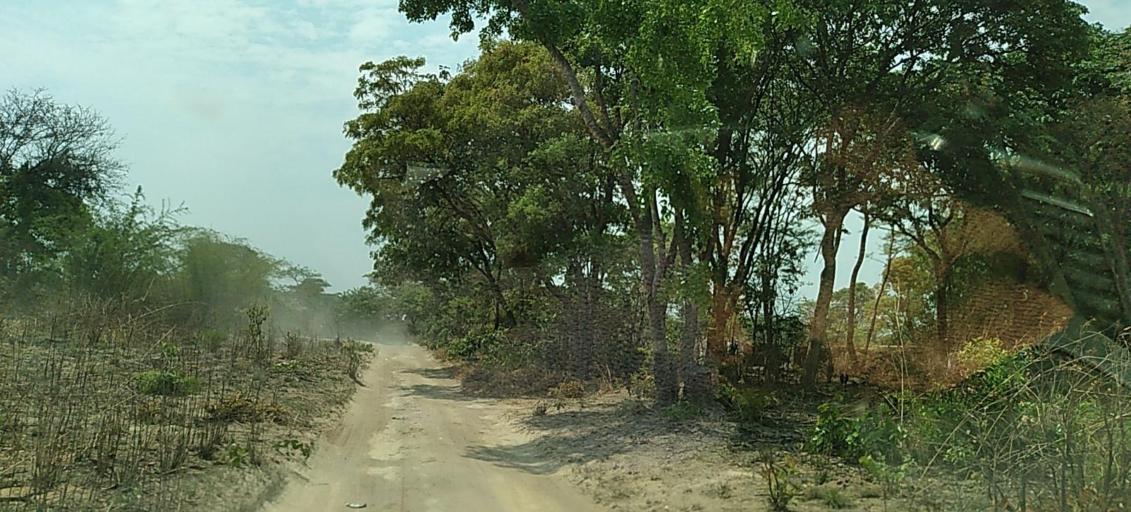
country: ZM
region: Copperbelt
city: Kalulushi
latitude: -12.9271
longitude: 28.1055
